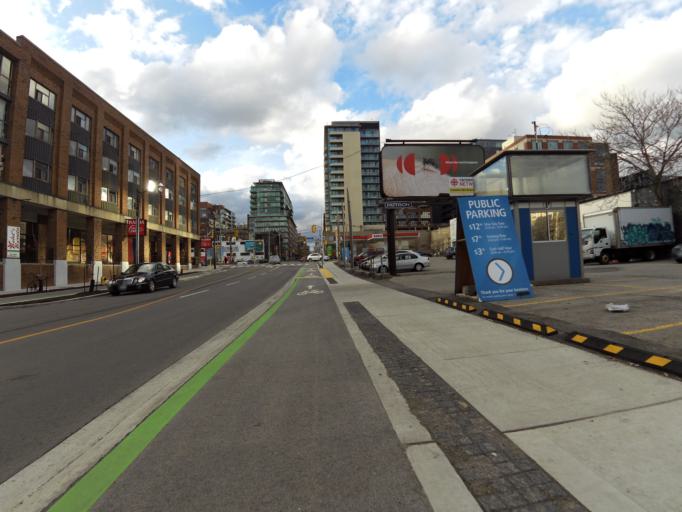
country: CA
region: Ontario
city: Toronto
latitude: 43.6498
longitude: -79.3675
